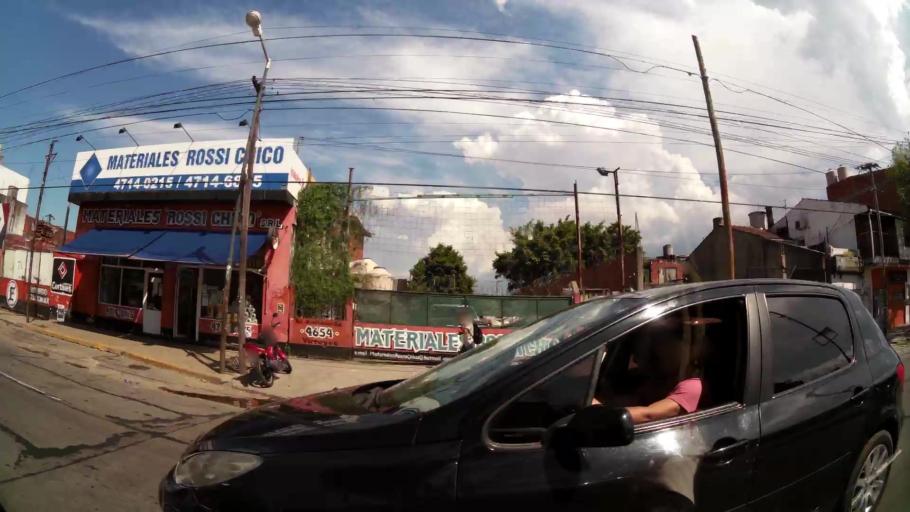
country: AR
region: Buenos Aires
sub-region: Partido de Tigre
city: Tigre
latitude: -34.4657
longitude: -58.5829
